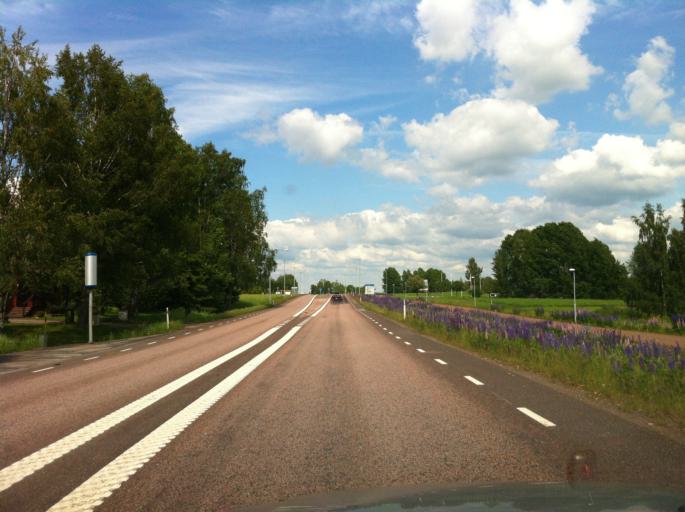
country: SE
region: Vaermland
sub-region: Sunne Kommun
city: Sunne
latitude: 59.8048
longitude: 13.1237
